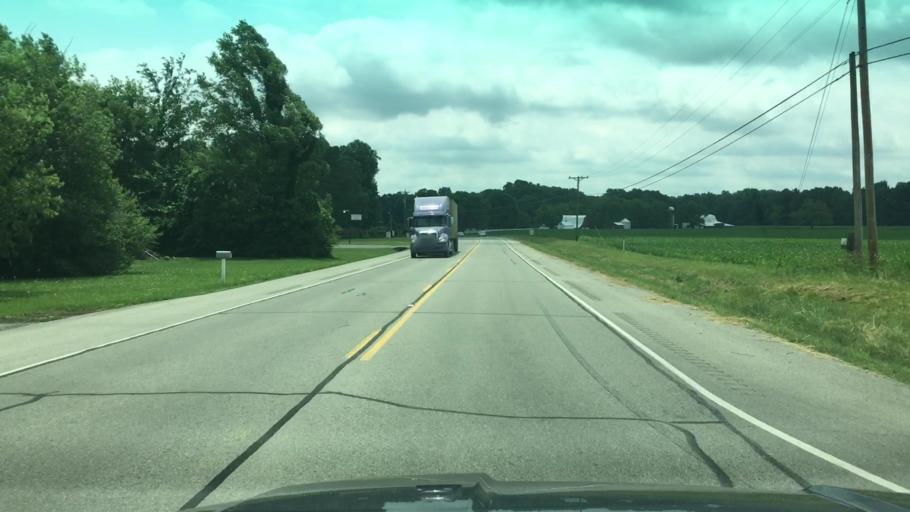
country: US
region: Tennessee
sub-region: Coffee County
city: New Union
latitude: 35.5281
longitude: -86.1583
